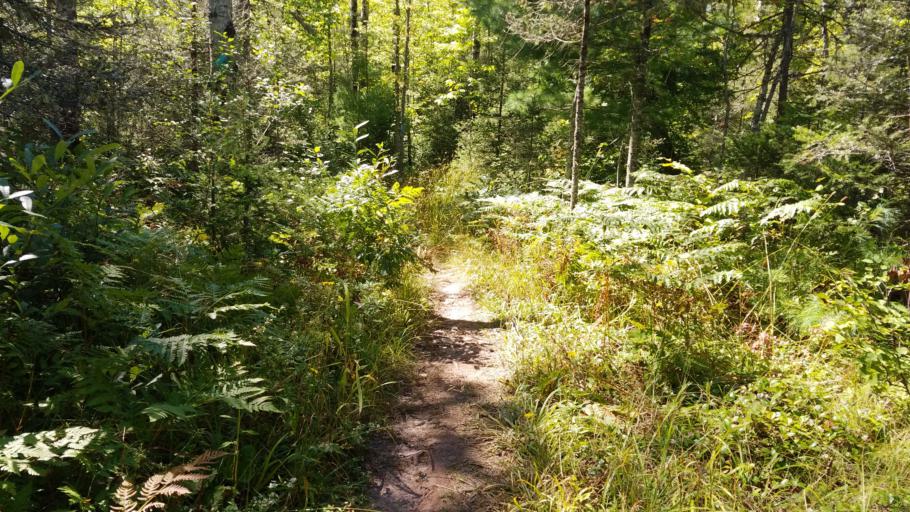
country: US
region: Michigan
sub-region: Ontonagon County
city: Ontonagon
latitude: 46.6501
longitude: -89.1632
